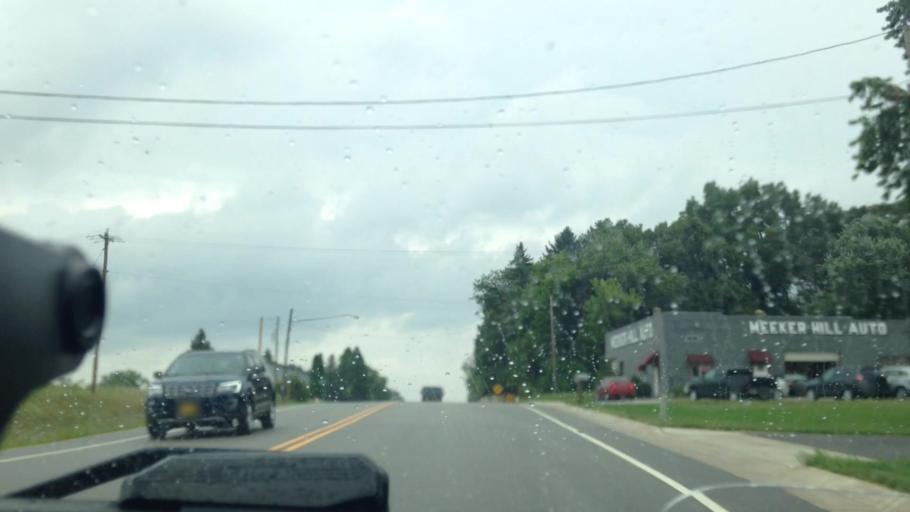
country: US
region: Wisconsin
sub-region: Washington County
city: Richfield
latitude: 43.2234
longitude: -88.1765
